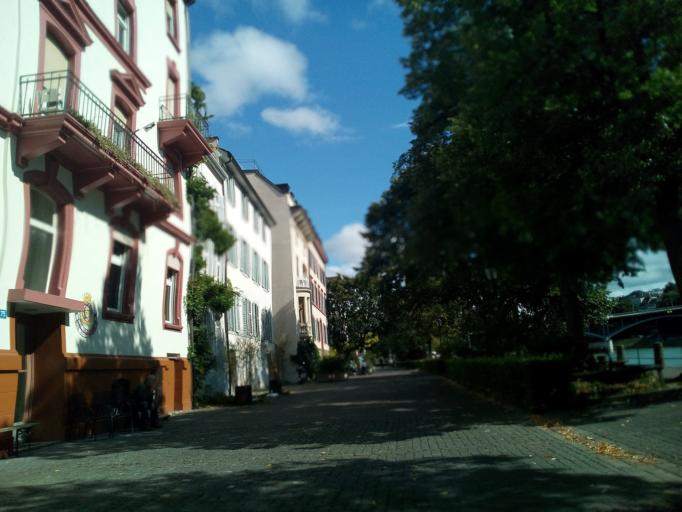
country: CH
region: Basel-City
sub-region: Basel-Stadt
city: Basel
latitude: 47.5590
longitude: 7.5930
